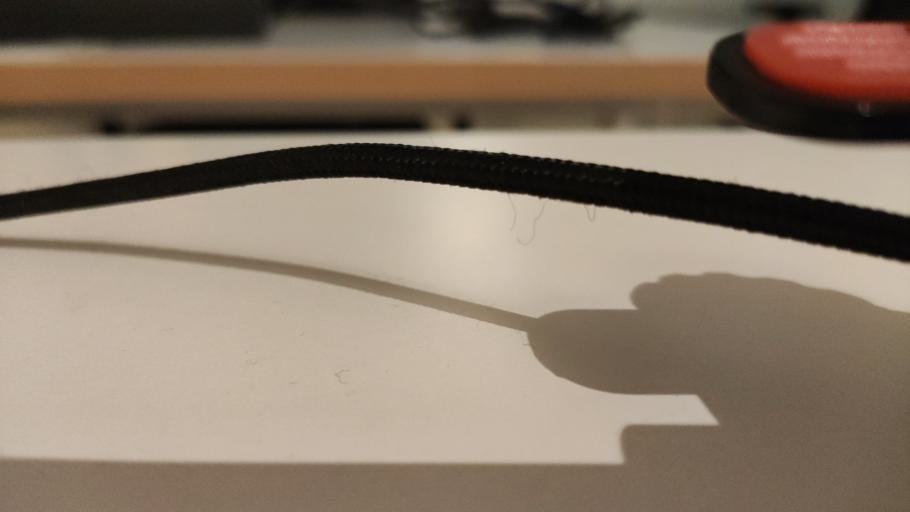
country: RU
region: Moskovskaya
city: Il'inskiy Pogost
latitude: 55.5321
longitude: 38.8725
